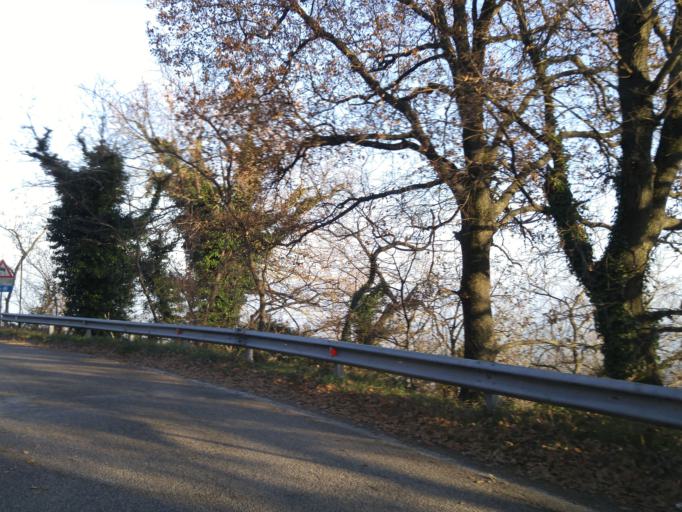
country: IT
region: The Marches
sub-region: Provincia di Pesaro e Urbino
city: Mombaroccio
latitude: 43.7837
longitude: 12.8554
